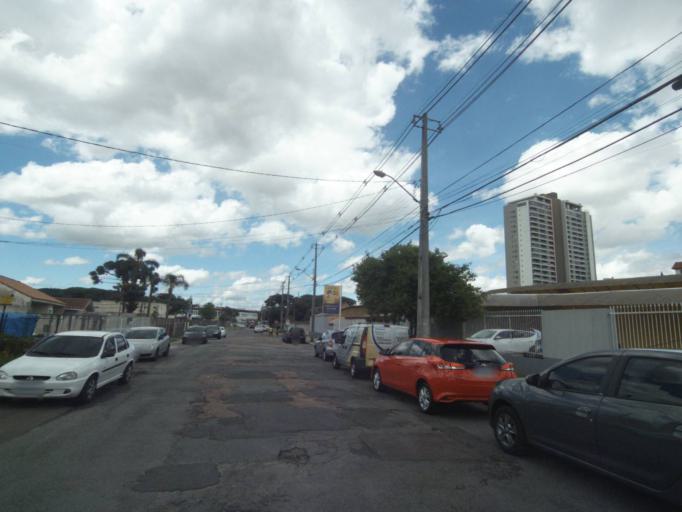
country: BR
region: Parana
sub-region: Curitiba
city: Curitiba
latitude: -25.4389
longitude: -49.3145
